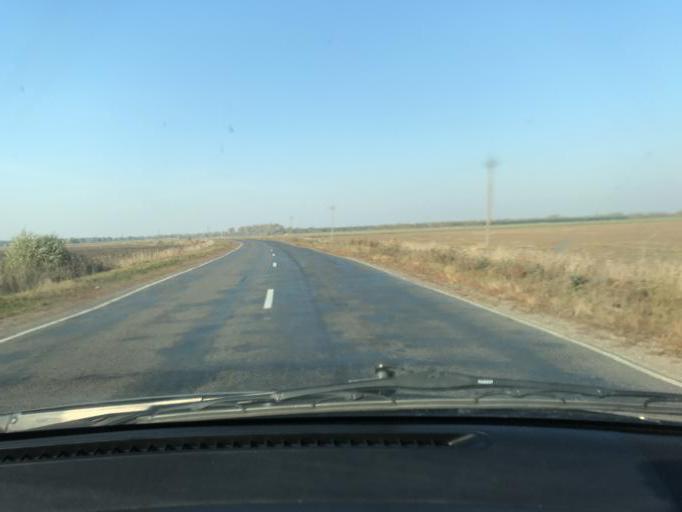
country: BY
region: Brest
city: Davyd-Haradok
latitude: 52.0648
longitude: 27.2540
